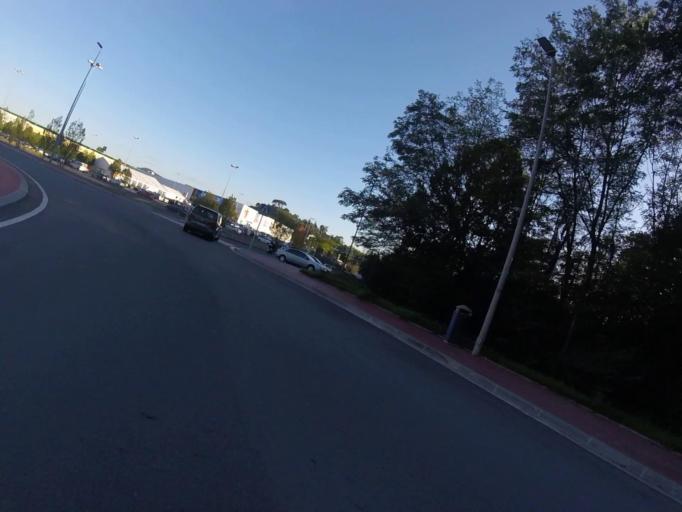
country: ES
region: Basque Country
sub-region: Provincia de Guipuzcoa
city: Lasarte
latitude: 43.2810
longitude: -2.0153
